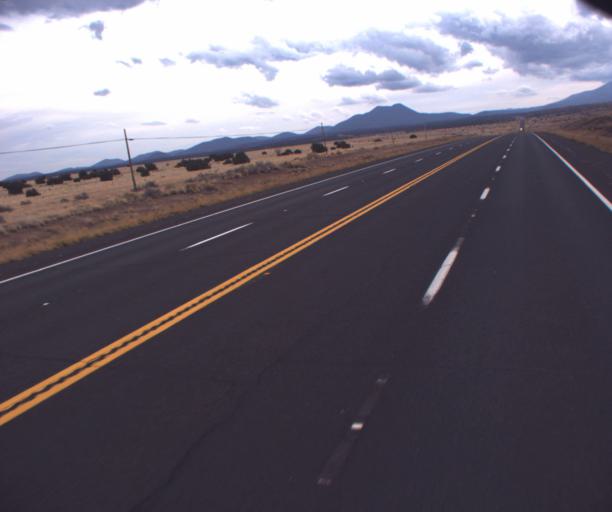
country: US
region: Arizona
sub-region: Coconino County
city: Flagstaff
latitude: 35.5700
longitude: -111.5321
